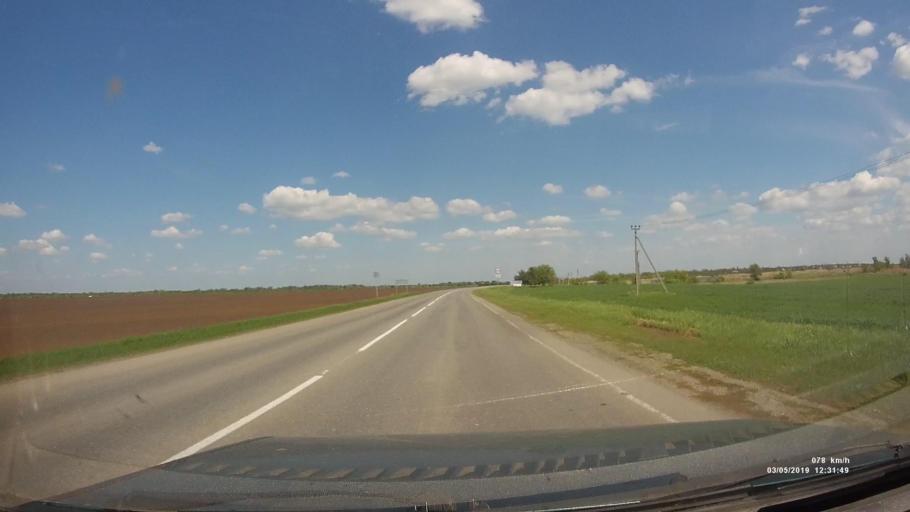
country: RU
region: Rostov
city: Semikarakorsk
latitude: 47.5074
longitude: 40.7515
